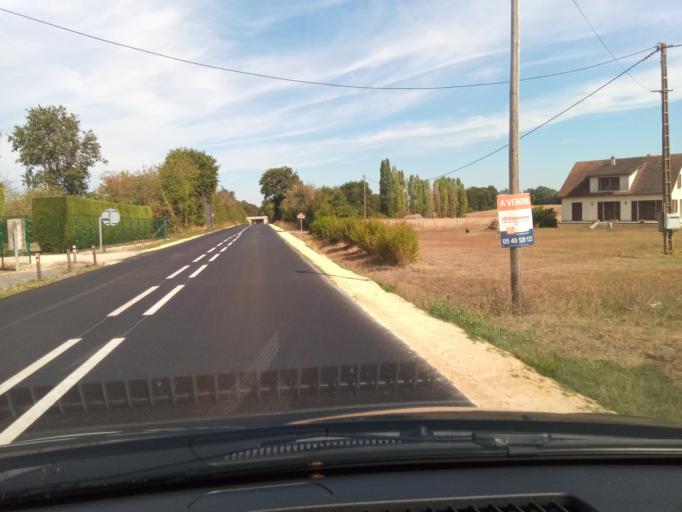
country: FR
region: Poitou-Charentes
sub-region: Departement de la Vienne
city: Terce
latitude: 46.4810
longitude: 0.5284
